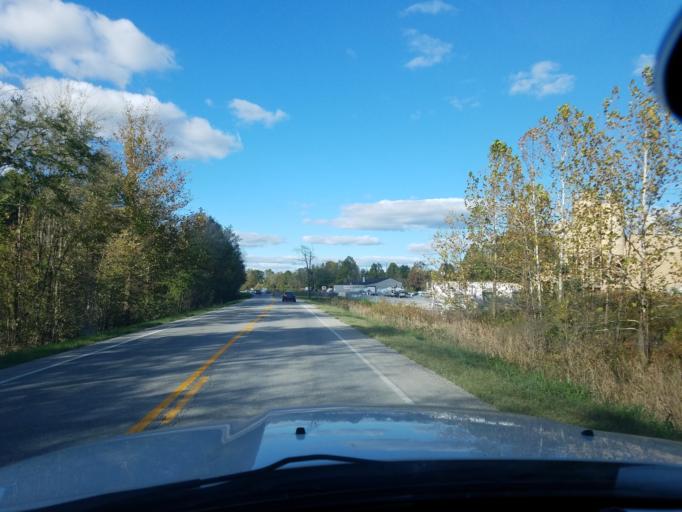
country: US
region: Kentucky
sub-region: Laurel County
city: London
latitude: 37.0696
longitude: -84.0588
